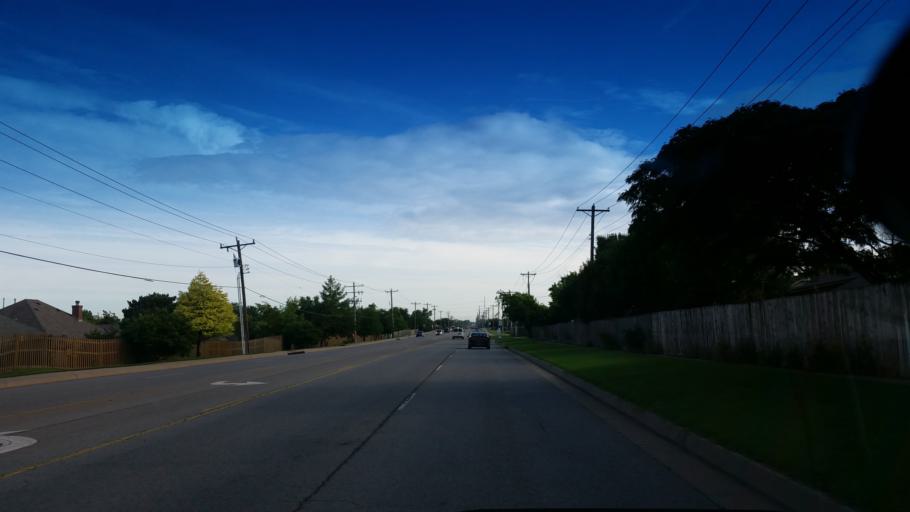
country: US
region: Oklahoma
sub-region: Oklahoma County
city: Edmond
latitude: 35.6331
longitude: -97.5138
